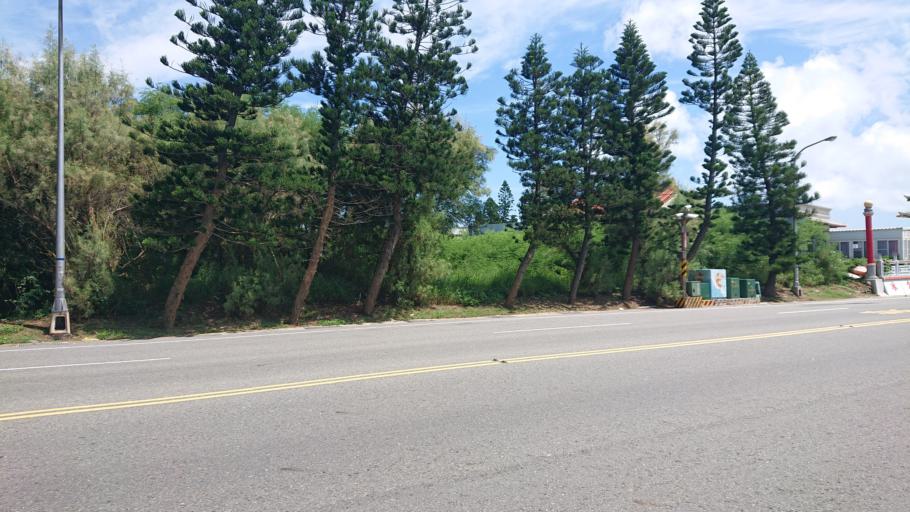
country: TW
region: Taiwan
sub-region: Penghu
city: Ma-kung
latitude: 23.6588
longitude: 119.5554
